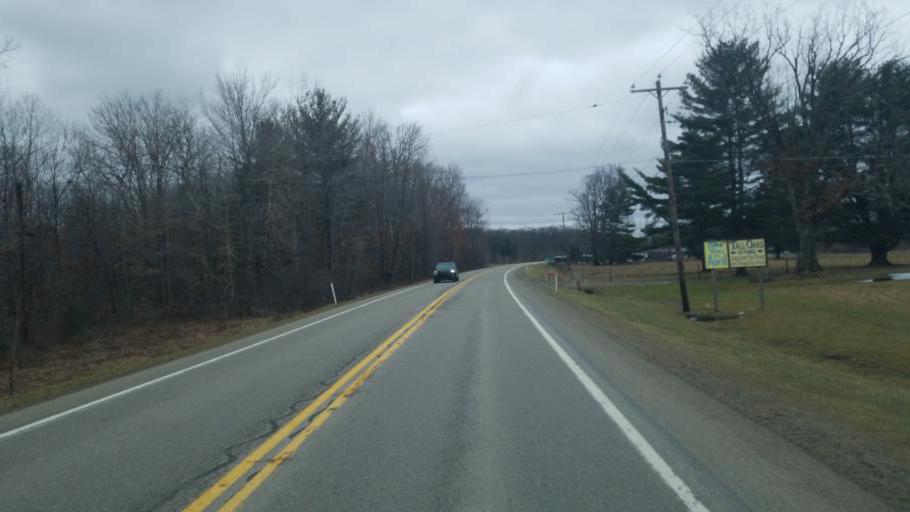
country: US
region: Pennsylvania
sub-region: Forest County
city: Marienville
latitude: 41.3982
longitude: -79.2571
